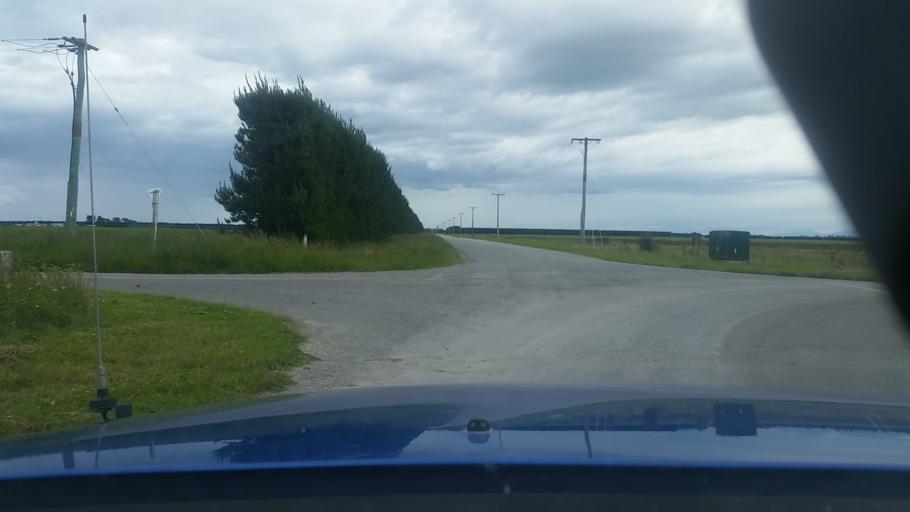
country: NZ
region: Canterbury
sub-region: Ashburton District
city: Rakaia
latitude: -43.9384
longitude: 172.0247
